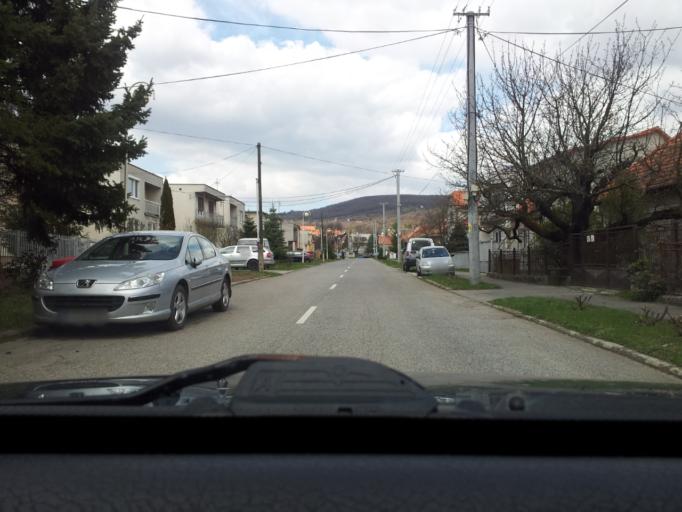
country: SK
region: Nitriansky
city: Tlmace
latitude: 48.2925
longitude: 18.5647
